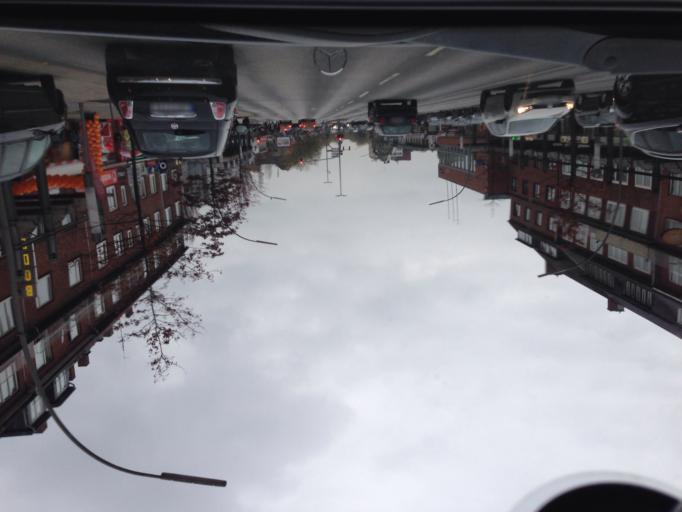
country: DE
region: Hamburg
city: Marienthal
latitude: 53.5708
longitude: 10.0627
